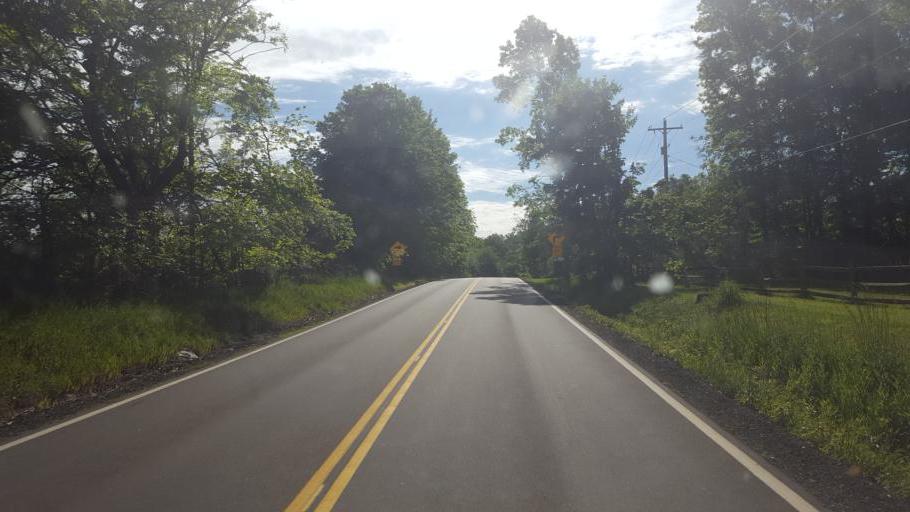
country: US
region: Ohio
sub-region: Medina County
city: Medina
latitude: 41.1065
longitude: -81.7935
